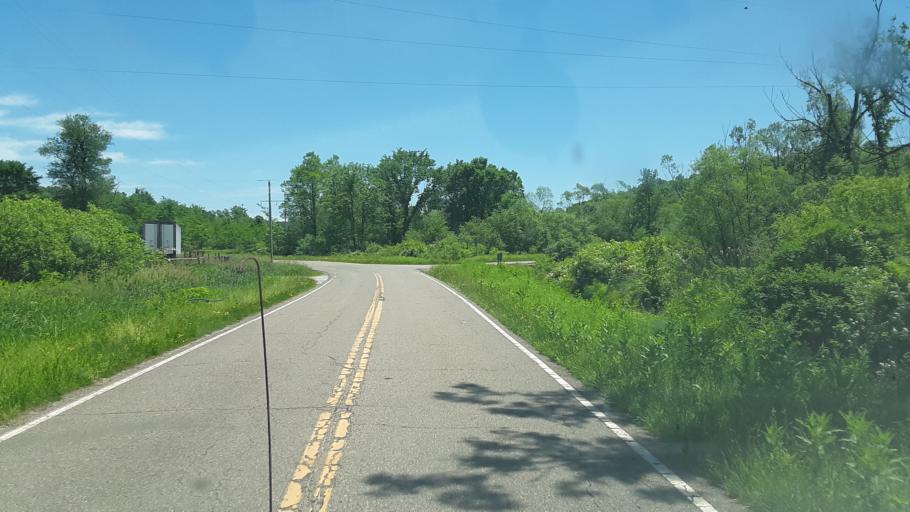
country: US
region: Ohio
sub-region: Coshocton County
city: Coshocton
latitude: 40.2895
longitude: -82.0034
